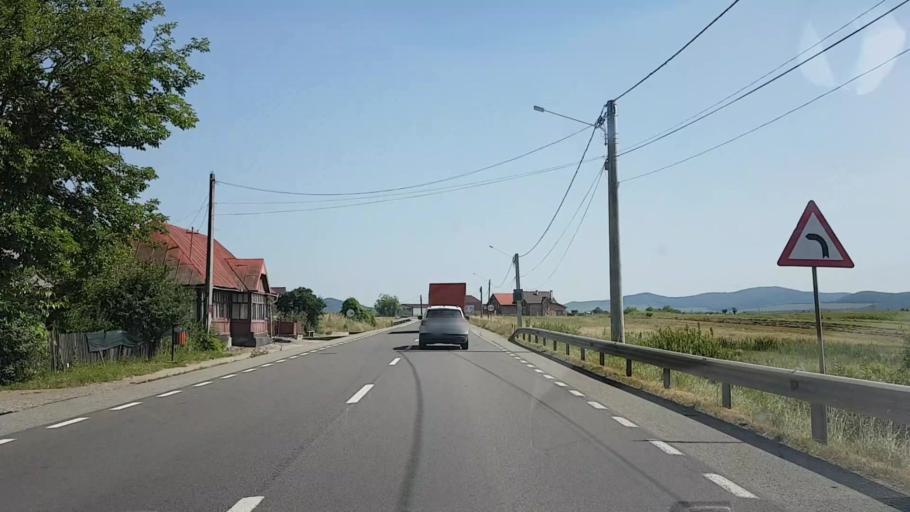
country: RO
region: Bistrita-Nasaud
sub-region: Comuna Sieu-Odorhei
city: Sieu-Odorhei
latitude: 47.1384
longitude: 24.3070
